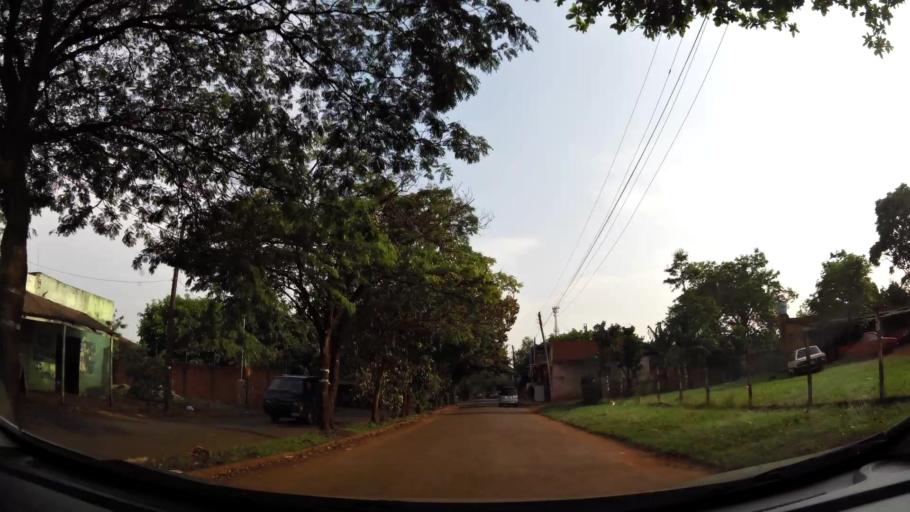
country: PY
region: Alto Parana
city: Ciudad del Este
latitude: -25.4909
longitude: -54.6774
